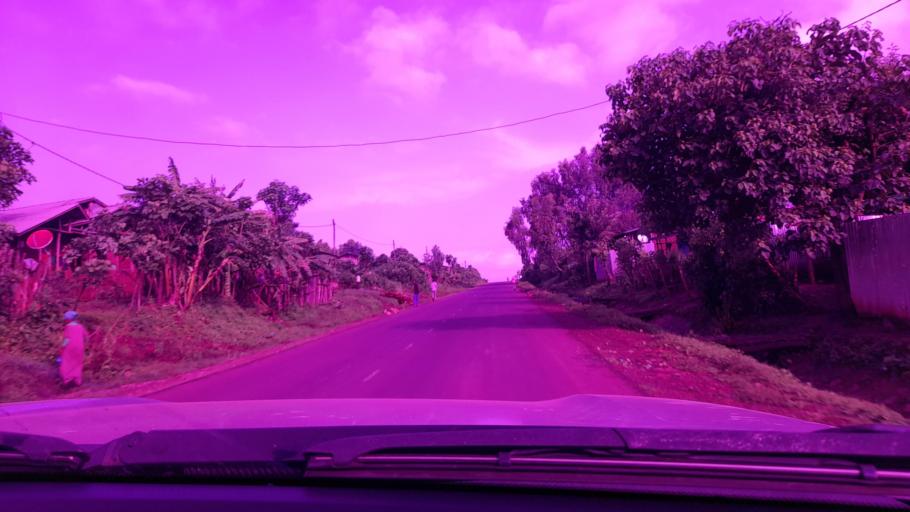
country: ET
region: Oromiya
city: Bedele
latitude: 8.1688
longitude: 36.4662
